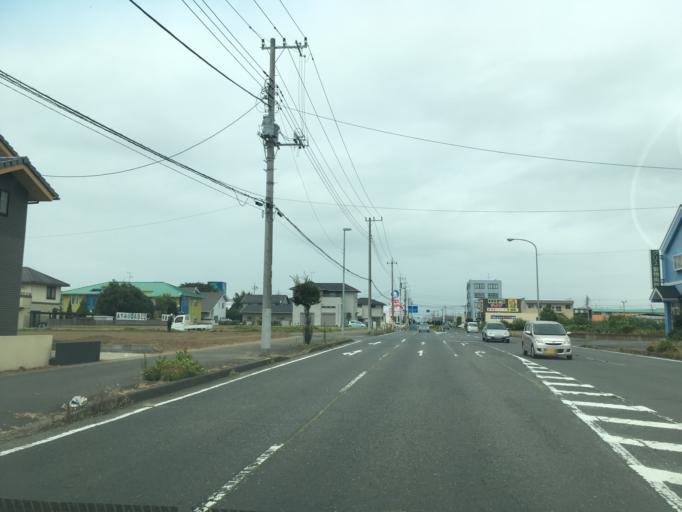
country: JP
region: Ibaraki
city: Hitachi-Naka
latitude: 36.3948
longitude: 140.5547
